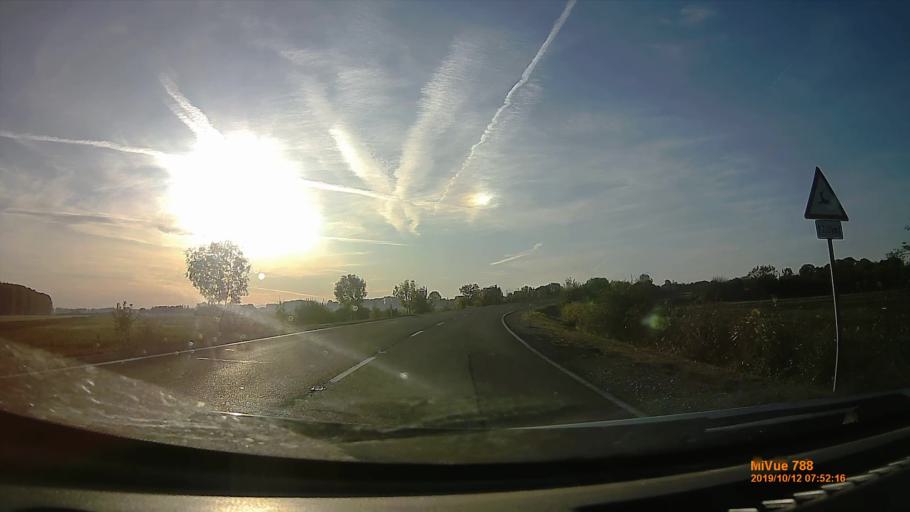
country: HU
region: Hajdu-Bihar
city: Biharkeresztes
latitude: 47.1385
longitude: 21.7363
